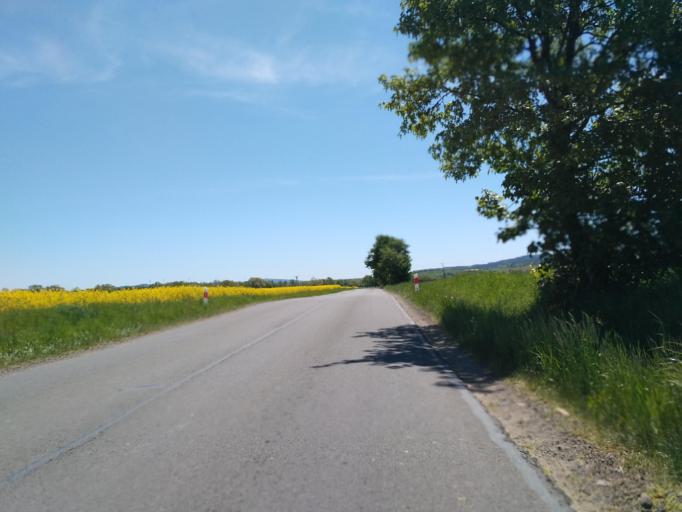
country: PL
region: Subcarpathian Voivodeship
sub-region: Powiat krosnienski
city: Sieniawa
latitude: 49.5497
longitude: 21.9422
